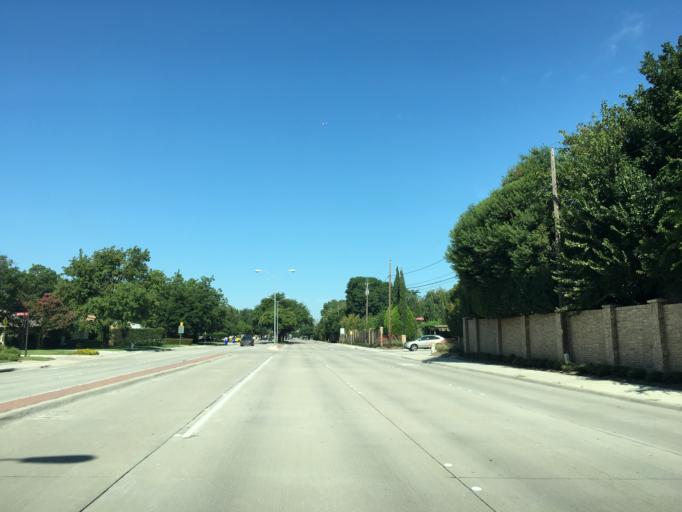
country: US
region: Texas
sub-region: Dallas County
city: Farmers Branch
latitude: 32.9244
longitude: -96.8761
